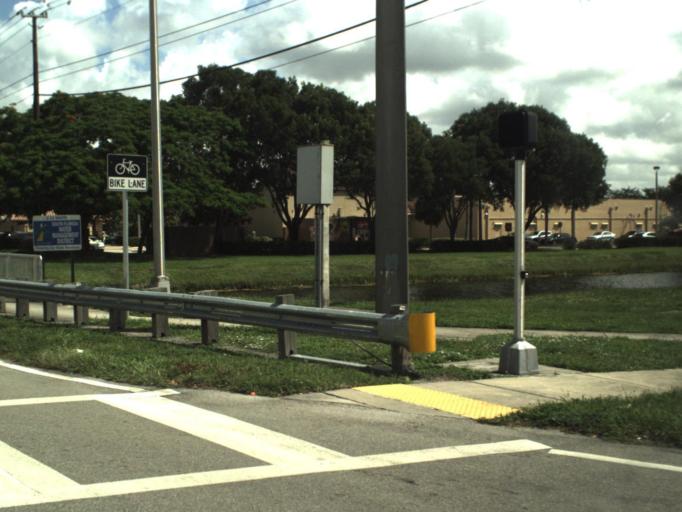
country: US
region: Florida
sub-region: Broward County
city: Sunshine Ranches
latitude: 26.0442
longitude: -80.3128
